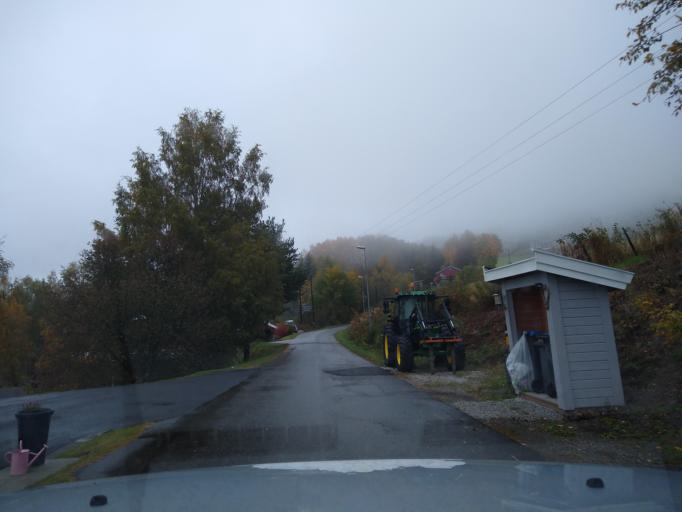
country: NO
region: Oppland
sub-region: Ringebu
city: Ringebu
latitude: 61.4487
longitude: 10.2097
